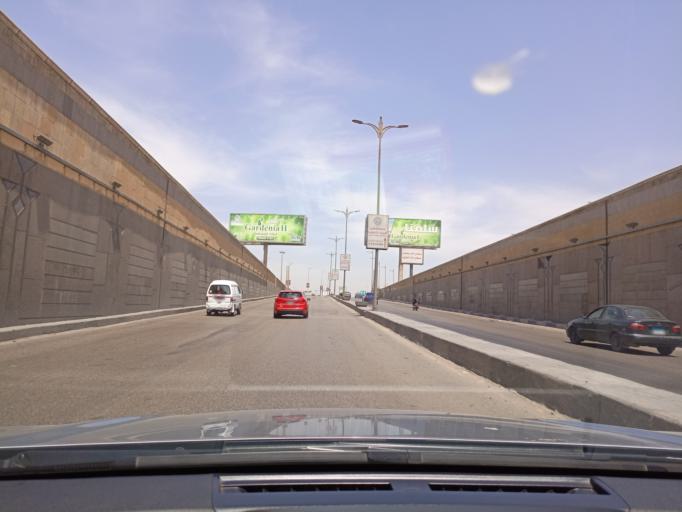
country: EG
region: Muhafazat al Qalyubiyah
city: Al Khankah
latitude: 30.1645
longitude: 31.4782
